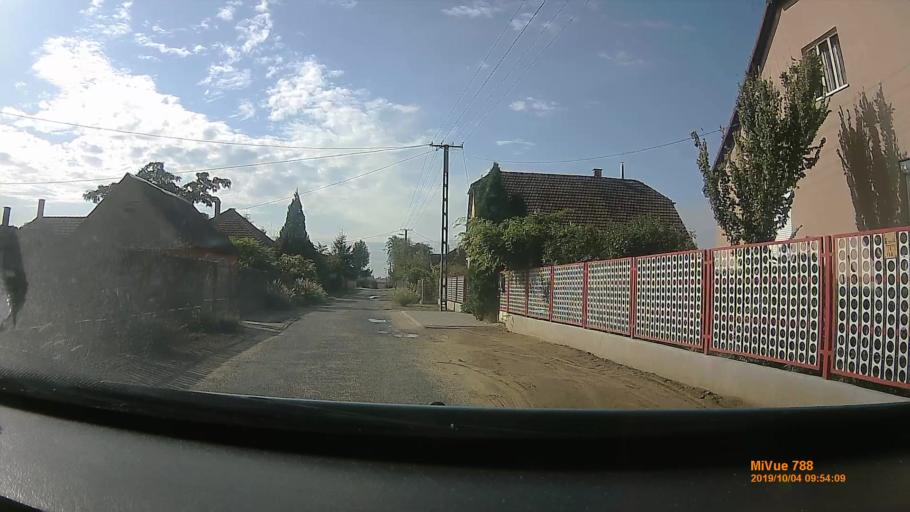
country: HU
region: Szabolcs-Szatmar-Bereg
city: Nyiregyhaza
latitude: 47.9414
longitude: 21.6635
